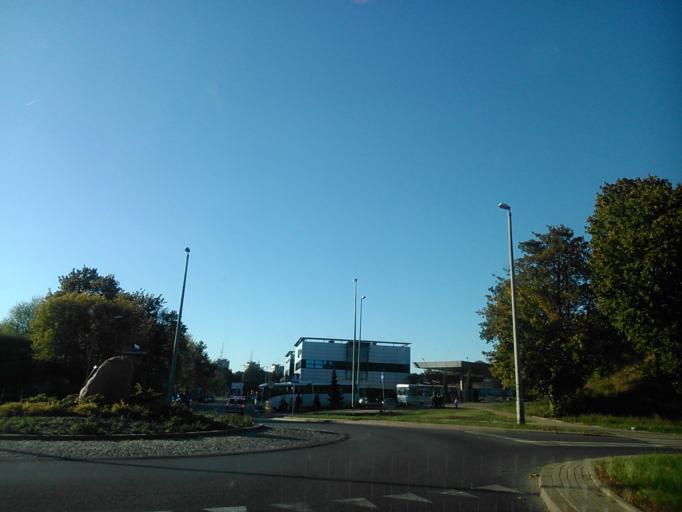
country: PL
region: Kujawsko-Pomorskie
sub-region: Torun
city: Torun
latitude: 53.0150
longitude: 18.6095
